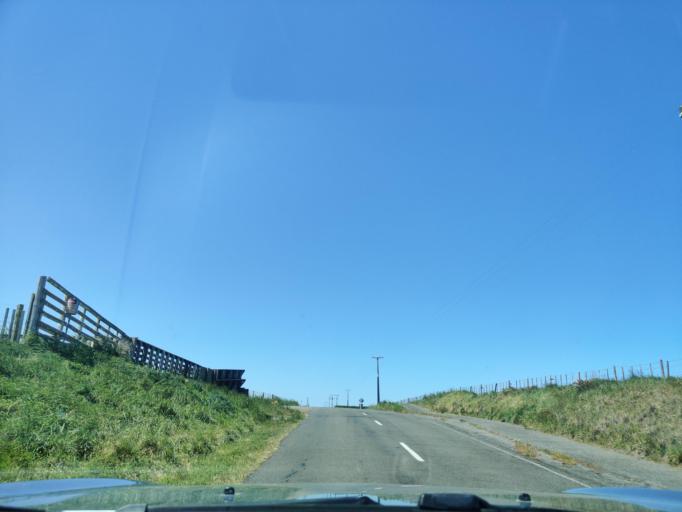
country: NZ
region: Taranaki
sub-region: South Taranaki District
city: Hawera
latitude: -39.6008
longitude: 174.2530
